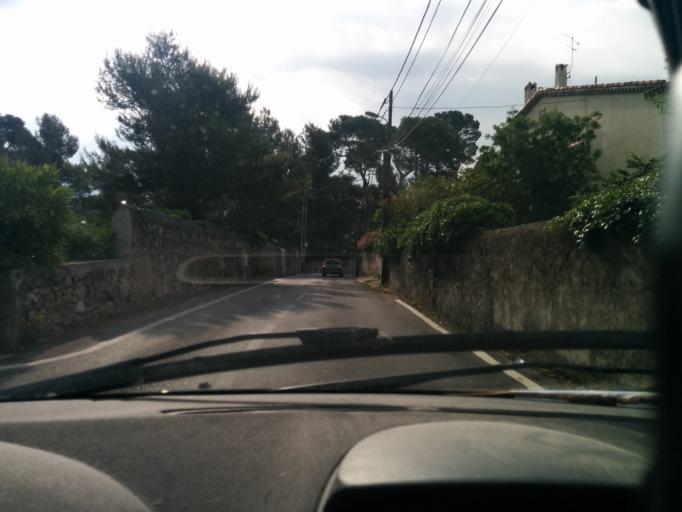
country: FR
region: Provence-Alpes-Cote d'Azur
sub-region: Departement des Bouches-du-Rhone
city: Marseille 12
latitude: 43.3199
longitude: 5.4465
